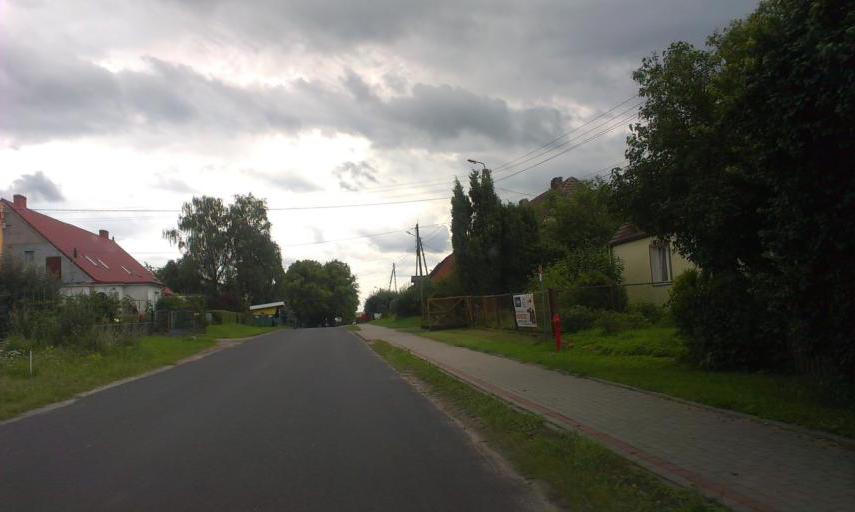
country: PL
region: West Pomeranian Voivodeship
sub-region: Powiat bialogardzki
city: Tychowo
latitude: 53.9368
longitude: 16.2393
